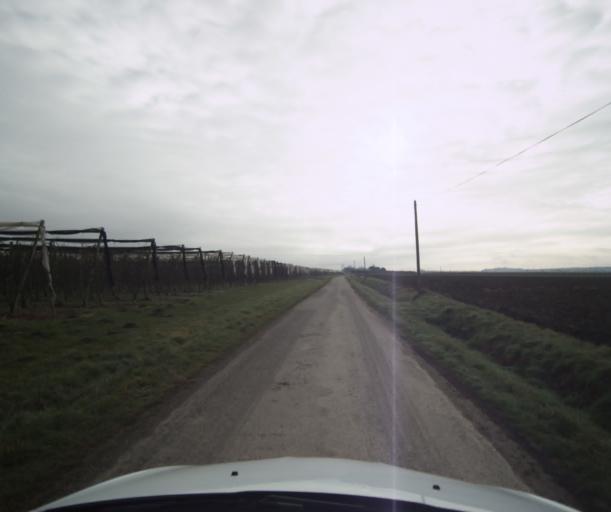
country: FR
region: Midi-Pyrenees
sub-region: Departement du Tarn-et-Garonne
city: Castelsarrasin
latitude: 44.0268
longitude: 1.1207
